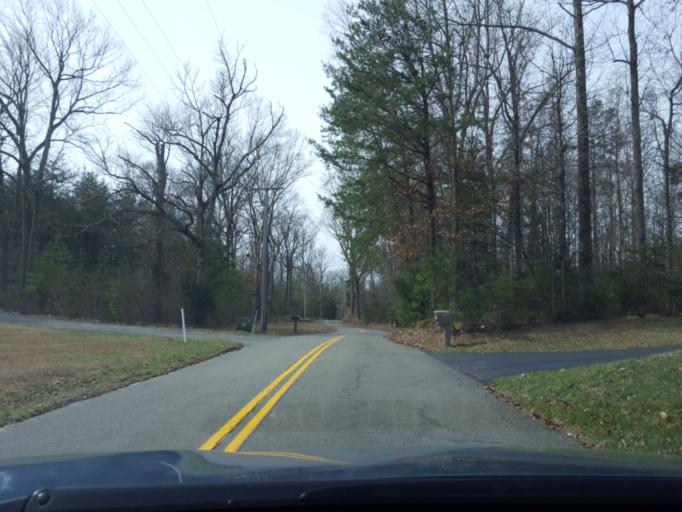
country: US
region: Maryland
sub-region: Calvert County
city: Lusby
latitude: 38.4119
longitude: -76.4331
